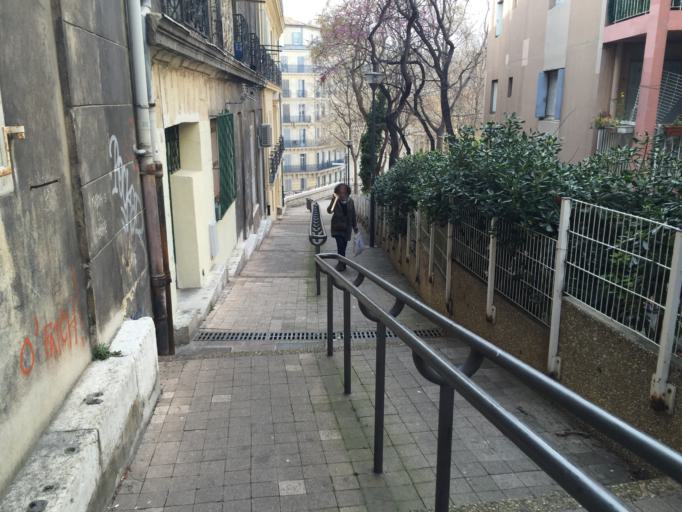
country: FR
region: Provence-Alpes-Cote d'Azur
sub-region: Departement des Bouches-du-Rhone
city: Marseille 02
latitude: 43.3006
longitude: 5.3718
